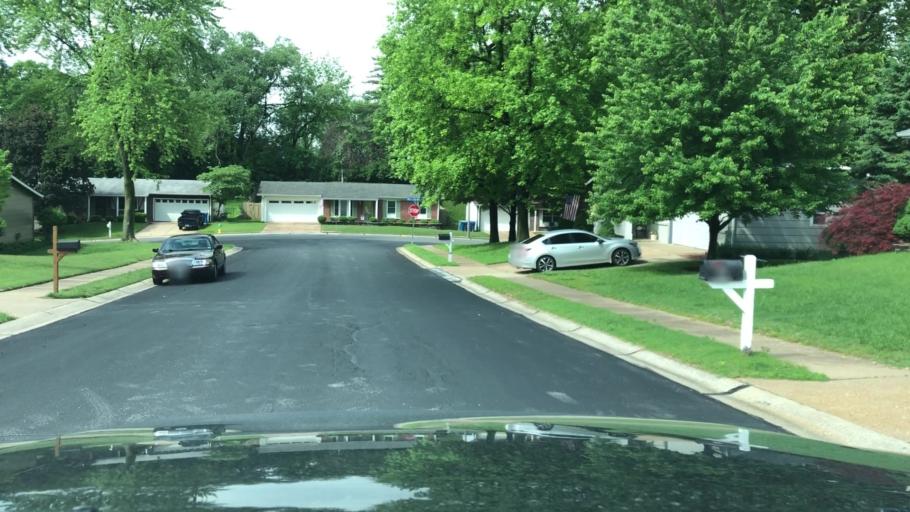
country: US
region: Missouri
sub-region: Saint Charles County
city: Saint Charles
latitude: 38.8109
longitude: -90.5089
